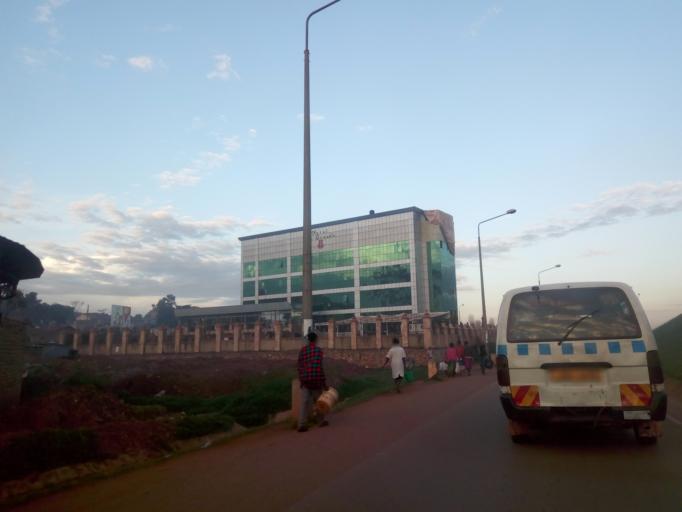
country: UG
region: Central Region
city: Kampala Central Division
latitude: 0.3495
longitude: 32.5646
